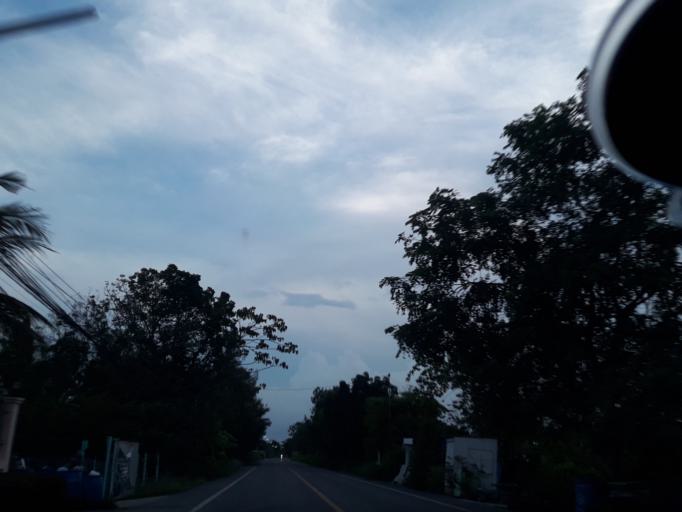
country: TH
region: Pathum Thani
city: Nong Suea
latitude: 14.1247
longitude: 100.8690
